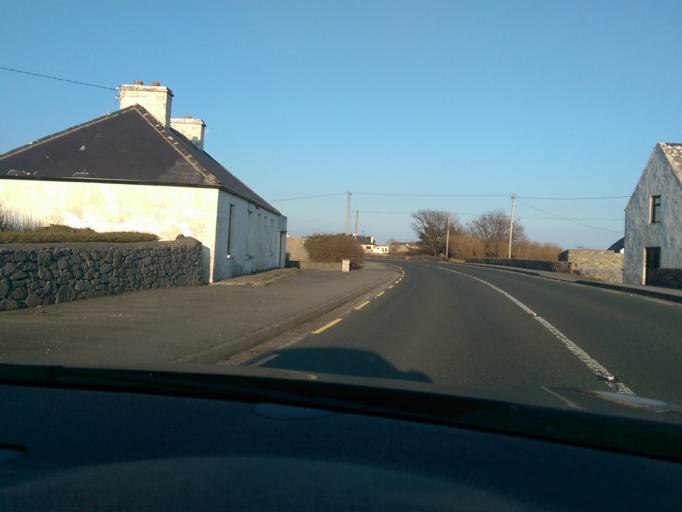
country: IE
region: Connaught
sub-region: County Galway
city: Oughterard
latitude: 53.2391
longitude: -9.4246
